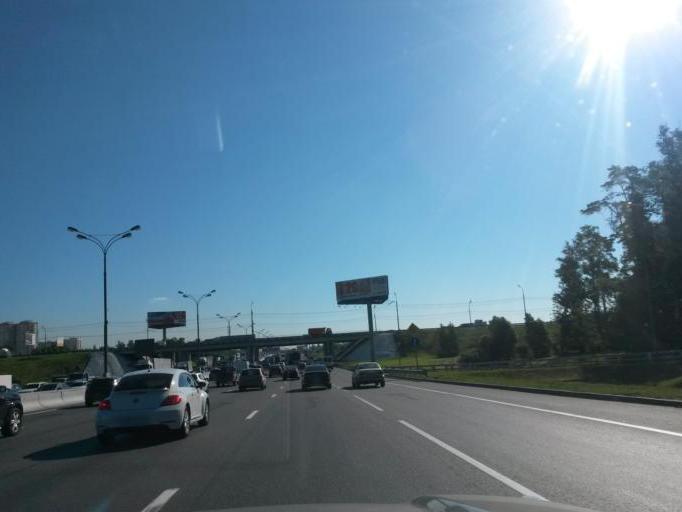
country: RU
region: Moscow
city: Biryulevo
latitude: 55.5748
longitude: 37.6854
